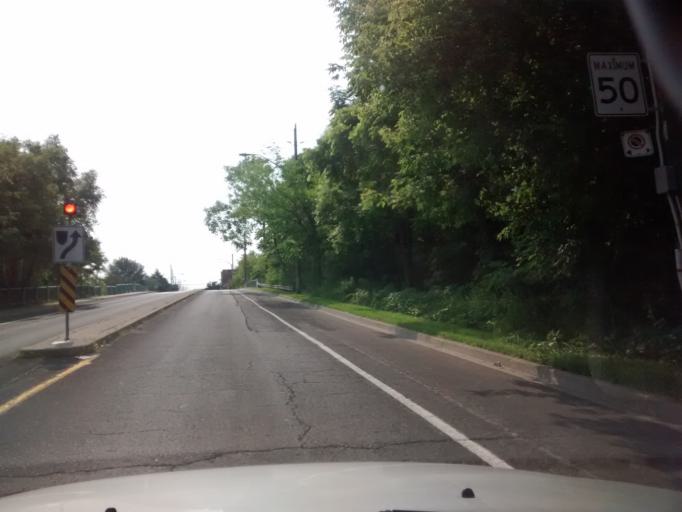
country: CA
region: Ontario
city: Hamilton
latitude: 43.2316
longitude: -79.8150
